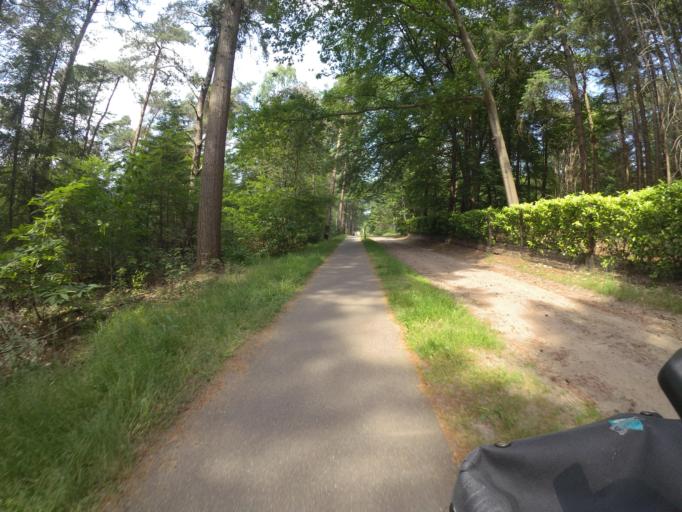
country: NL
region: Overijssel
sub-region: Gemeente Twenterand
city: Den Ham
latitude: 52.3732
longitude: 6.4316
